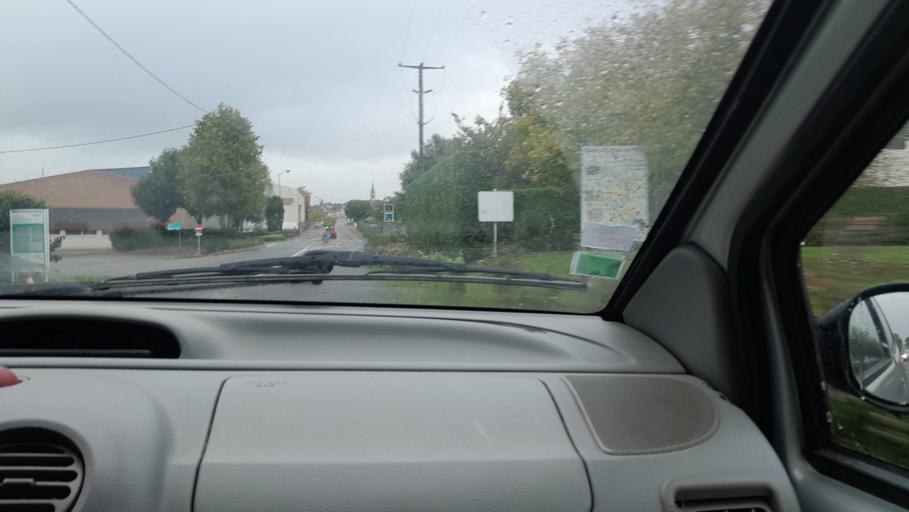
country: FR
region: Pays de la Loire
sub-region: Departement de la Mayenne
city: Congrier
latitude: 47.8363
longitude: -1.1395
